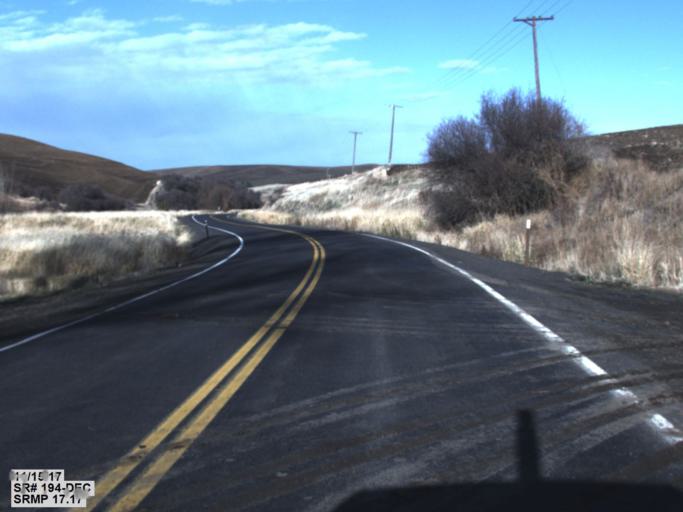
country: US
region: Washington
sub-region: Whitman County
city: Pullman
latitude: 46.7201
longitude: -117.2825
